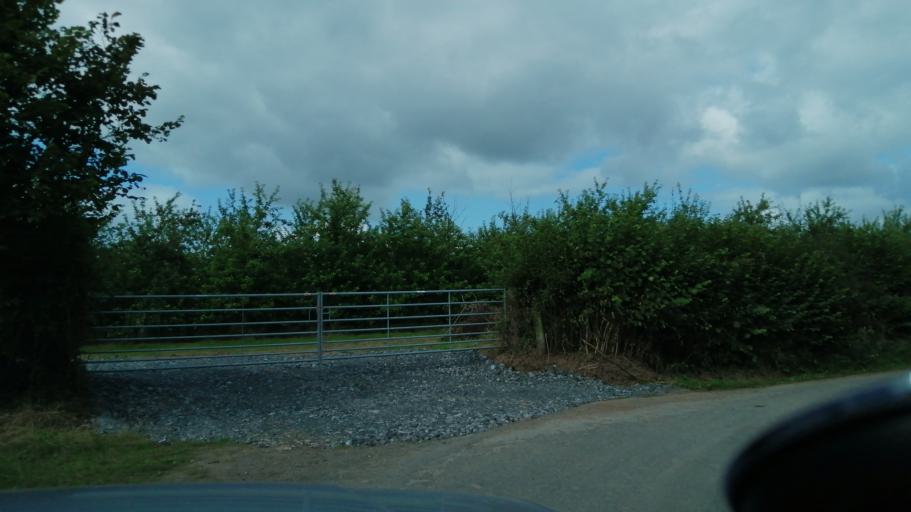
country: GB
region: England
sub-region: Herefordshire
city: Kinnersley
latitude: 52.1332
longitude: -2.9465
